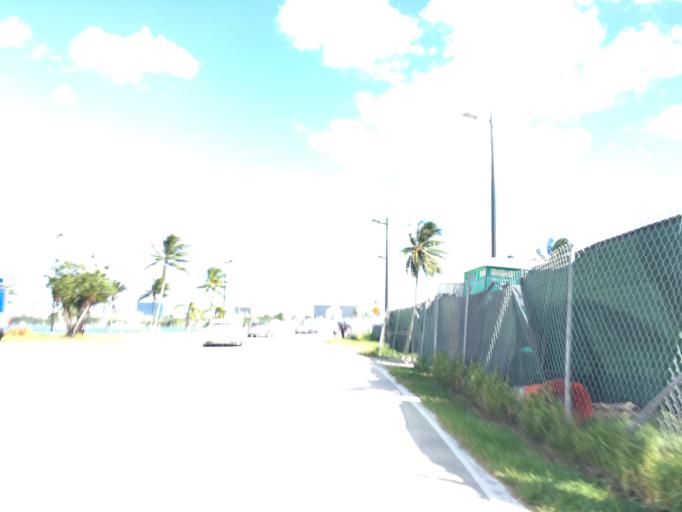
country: US
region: Florida
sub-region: Miami-Dade County
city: Bay Harbor Islands
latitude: 25.8876
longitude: -80.1448
